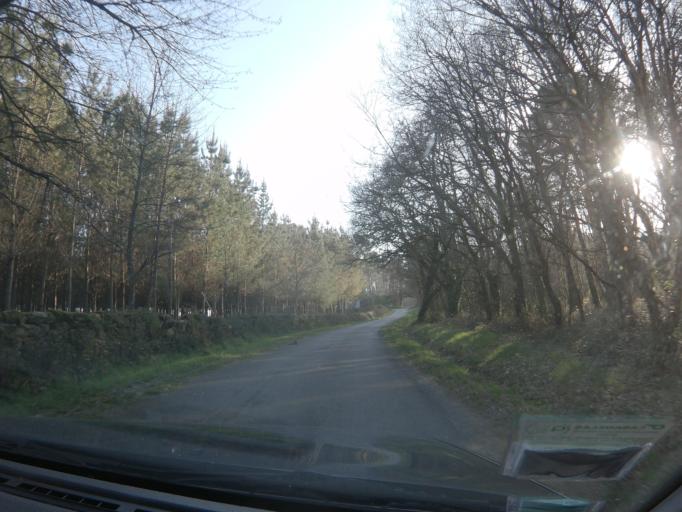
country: ES
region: Galicia
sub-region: Provincia de Lugo
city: Corgo
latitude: 42.9381
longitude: -7.4445
